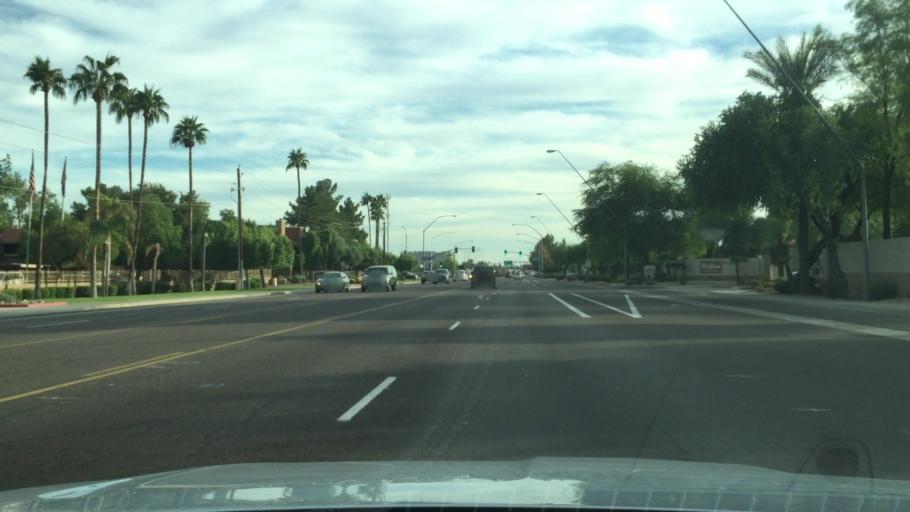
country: US
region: Arizona
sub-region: Maricopa County
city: Gilbert
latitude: 33.3919
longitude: -111.7539
